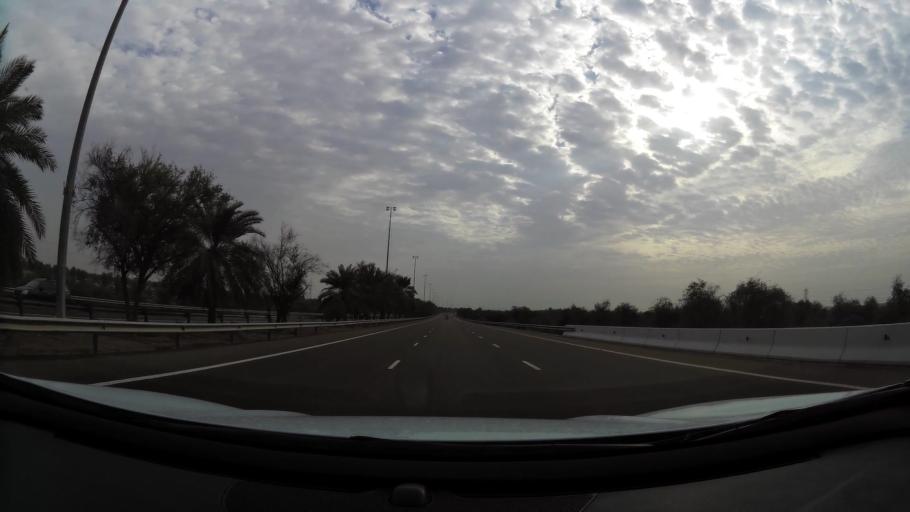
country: AE
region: Abu Dhabi
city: Al Ain
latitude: 24.1789
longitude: 55.1550
